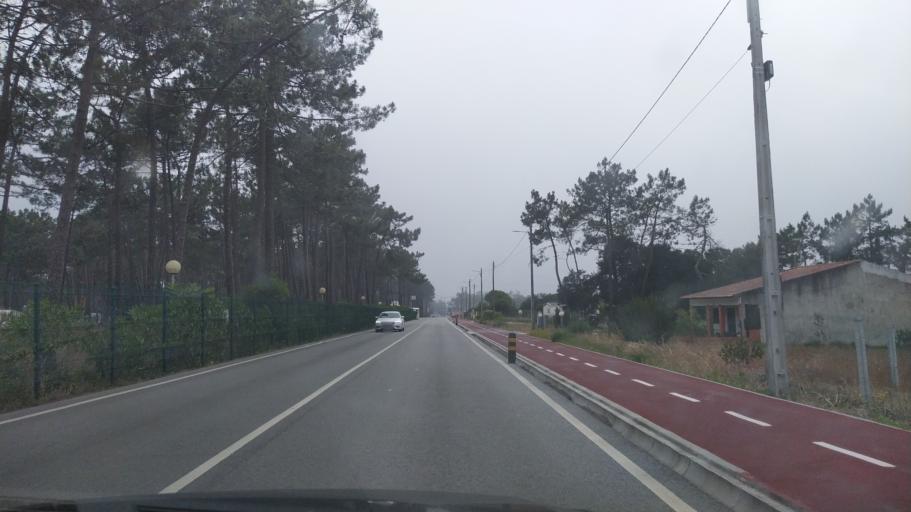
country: PT
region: Aveiro
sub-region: Ilhavo
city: Gafanha da Encarnacao
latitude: 40.5600
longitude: -8.7441
